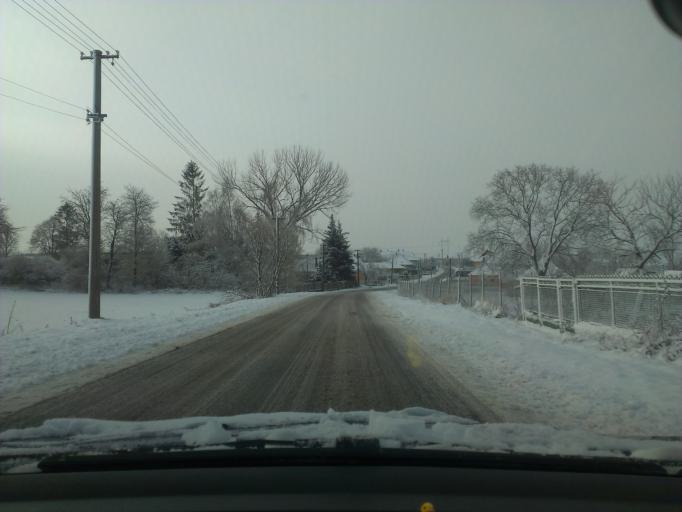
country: SK
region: Nitriansky
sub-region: Okres Nitra
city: Nitra
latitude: 48.4633
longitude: 17.9856
